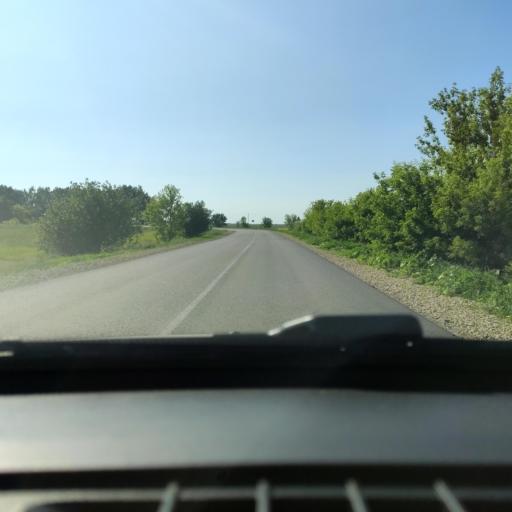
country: RU
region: Voronezj
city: Anna
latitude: 51.6476
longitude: 40.3718
